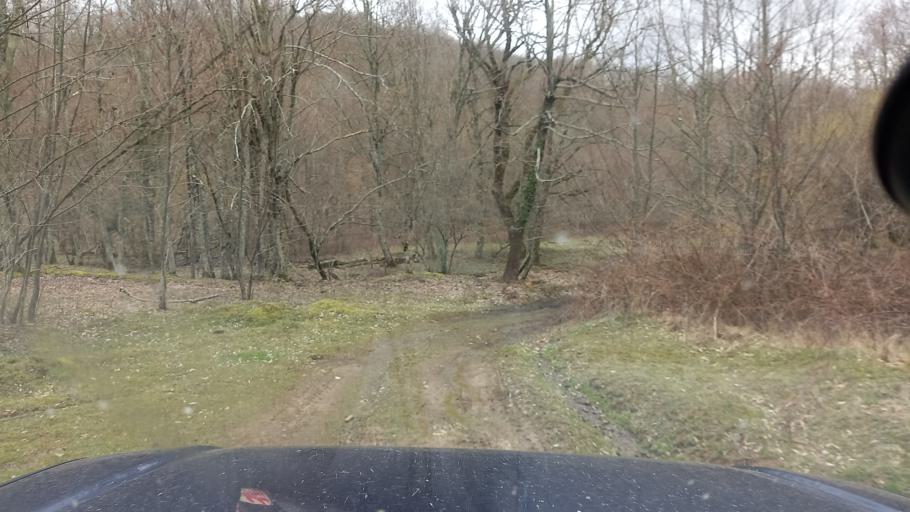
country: RU
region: Krasnodarskiy
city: Pshada
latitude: 44.4886
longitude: 38.3947
